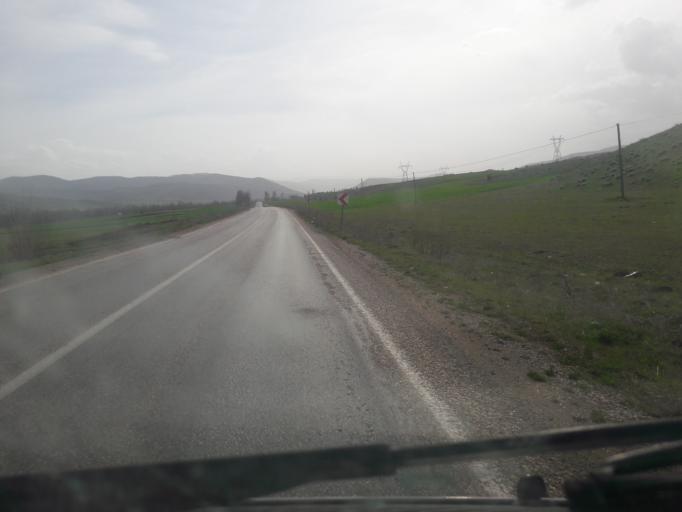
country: TR
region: Gumushane
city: Kelkit
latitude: 40.1380
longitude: 39.3853
